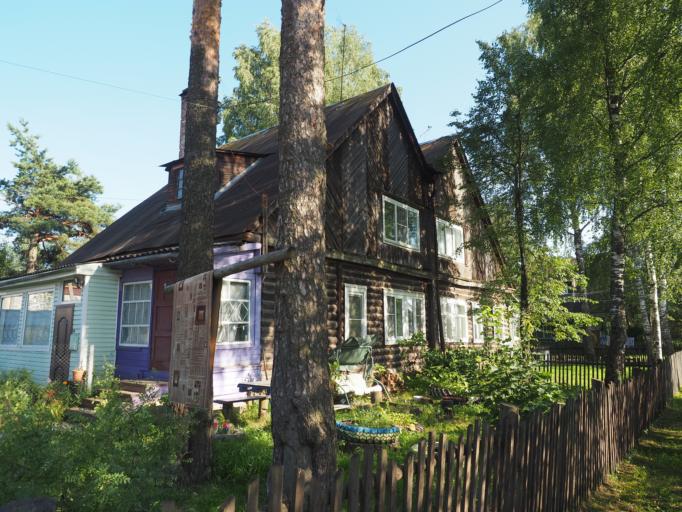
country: RU
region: Vologda
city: Chagoda
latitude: 59.1671
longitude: 35.3326
